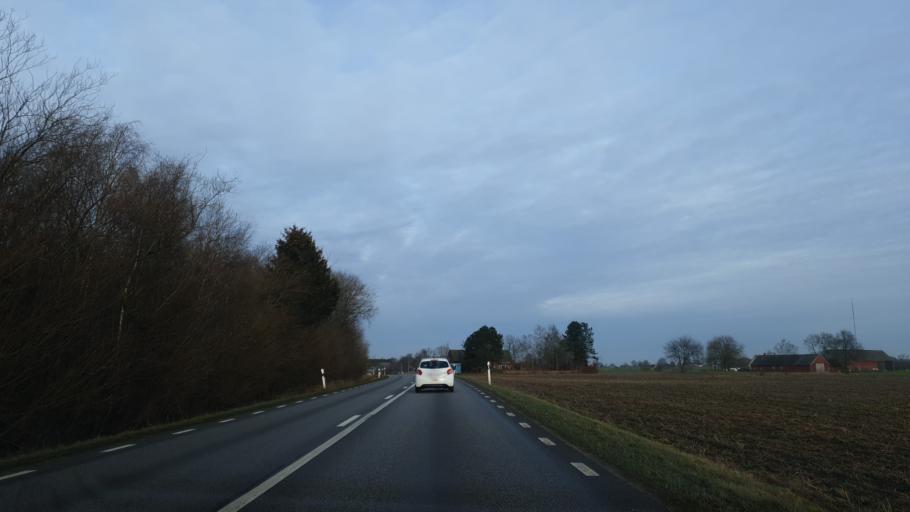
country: SE
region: Skane
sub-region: Horby Kommun
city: Hoerby
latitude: 55.7818
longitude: 13.6765
